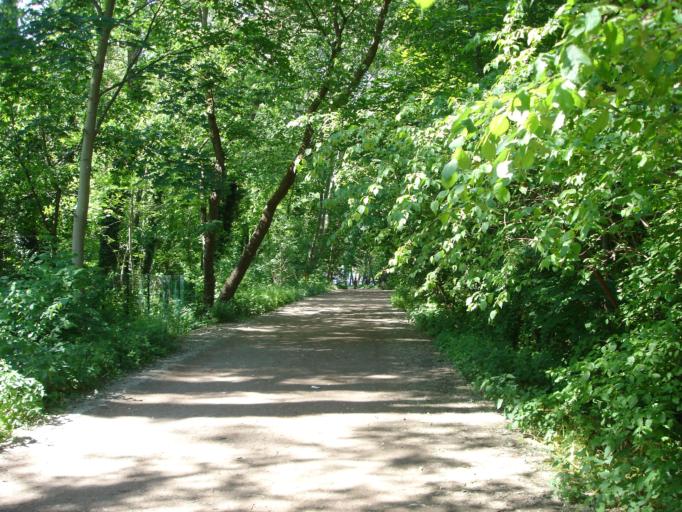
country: DE
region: Berlin
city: Plaenterwald
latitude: 52.4869
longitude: 13.4853
